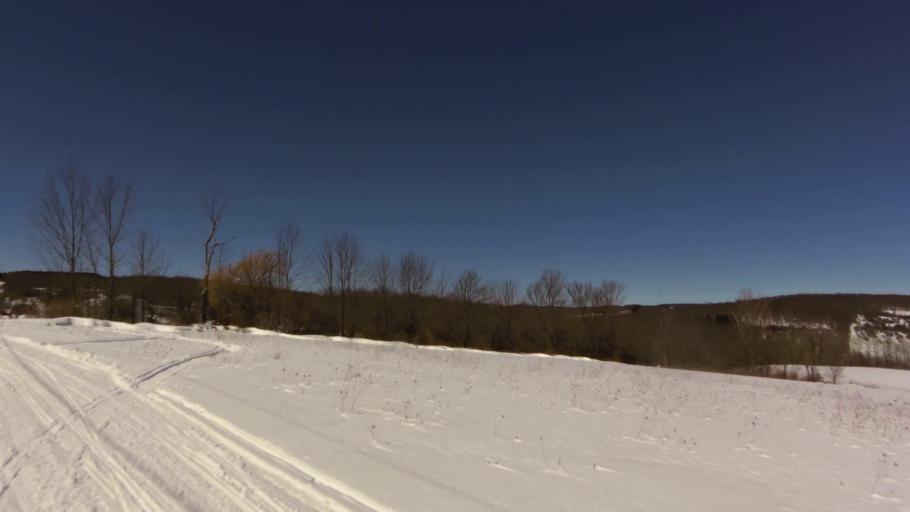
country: US
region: New York
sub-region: Allegany County
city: Houghton
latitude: 42.4086
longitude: -78.2795
